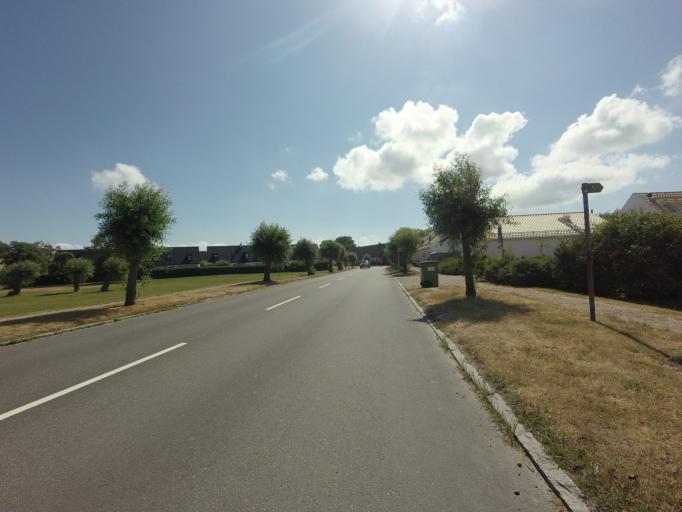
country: SE
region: Skane
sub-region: Vellinge Kommun
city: Skanor med Falsterbo
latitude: 55.4188
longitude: 12.8511
